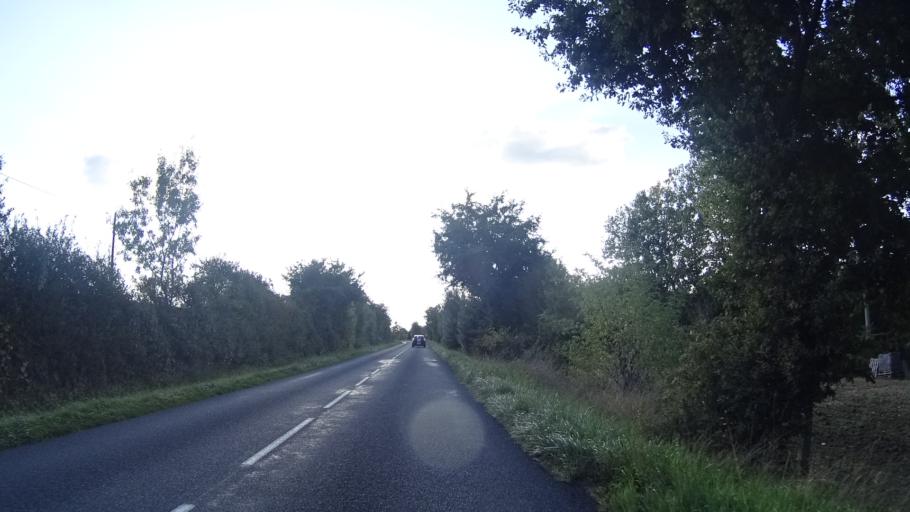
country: FR
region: Pays de la Loire
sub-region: Departement de Maine-et-Loire
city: Drain
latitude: 47.3448
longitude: -1.1959
